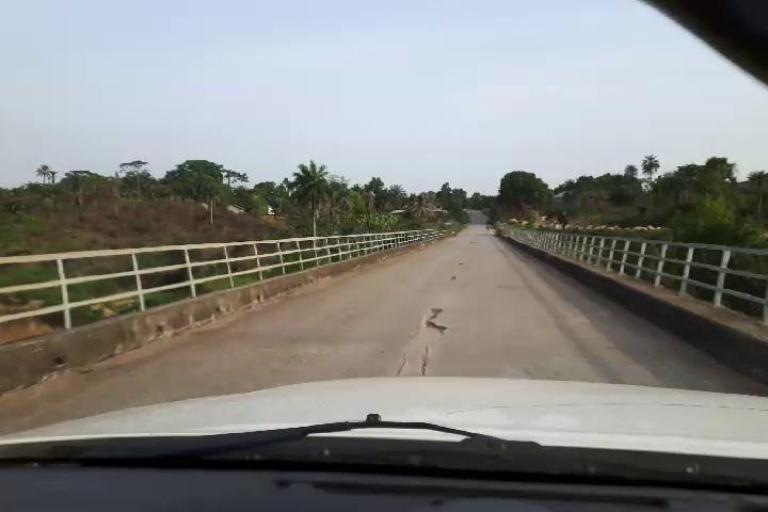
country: SL
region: Eastern Province
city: Blama
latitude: 7.9184
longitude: -11.4250
